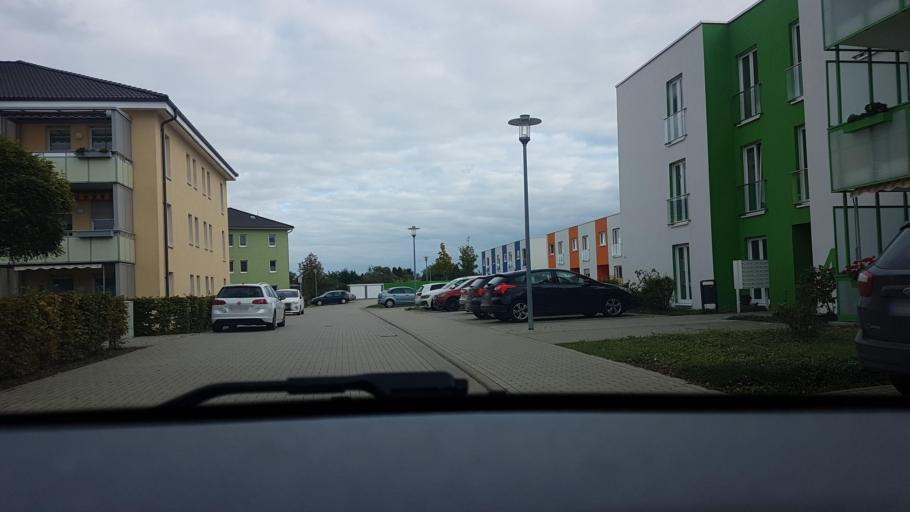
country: DE
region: Saxony-Anhalt
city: Bernburg
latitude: 51.7799
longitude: 11.7378
